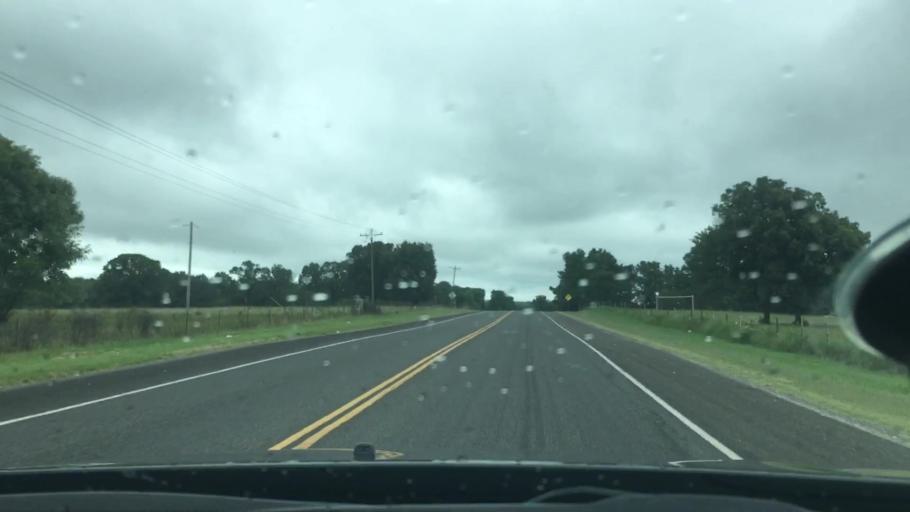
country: US
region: Oklahoma
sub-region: Sequoyah County
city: Vian
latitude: 35.5709
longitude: -94.9852
